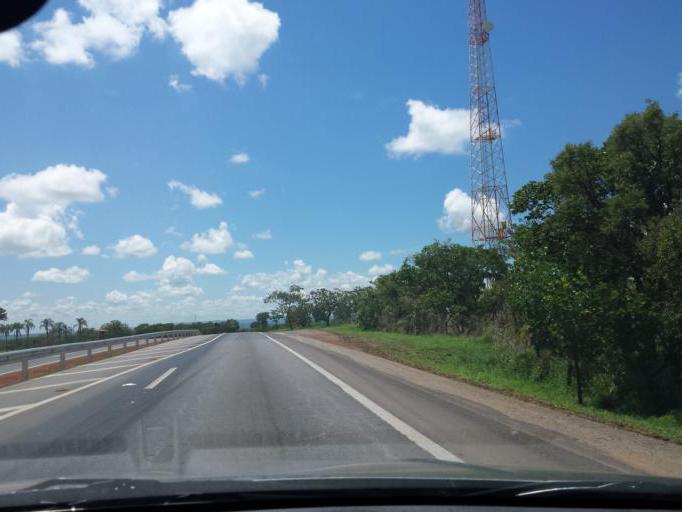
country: BR
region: Goias
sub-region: Luziania
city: Luziania
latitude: -16.3615
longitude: -47.8299
